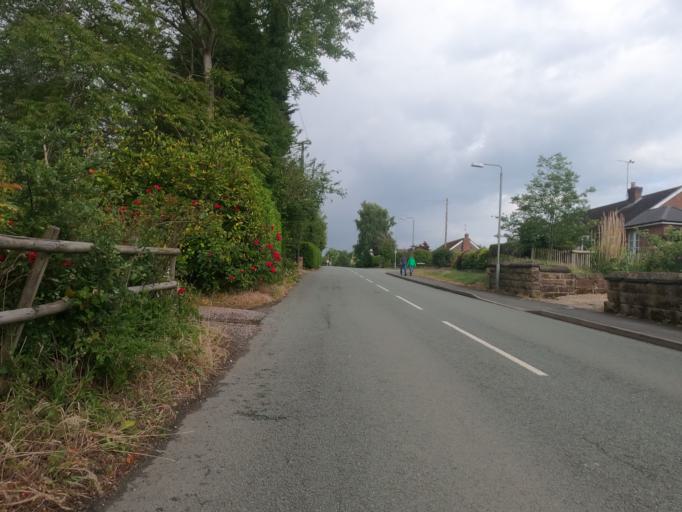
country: GB
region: England
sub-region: Cheshire West and Chester
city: Cuddington
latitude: 53.2405
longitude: -2.6039
